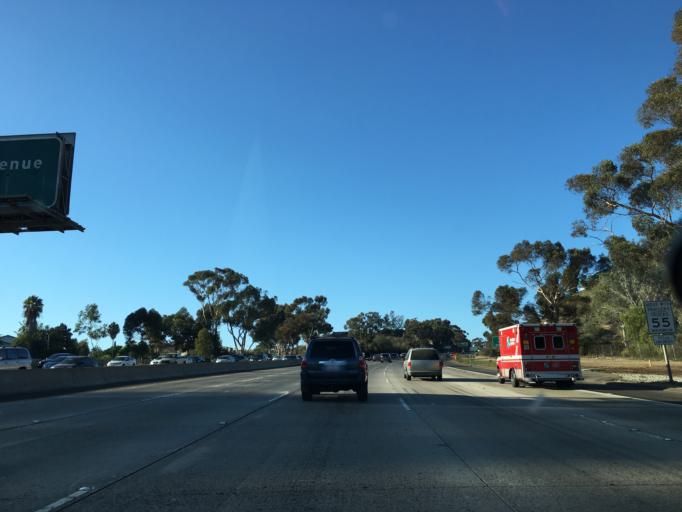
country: US
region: California
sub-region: San Diego County
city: San Diego
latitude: 32.7796
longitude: -117.1628
